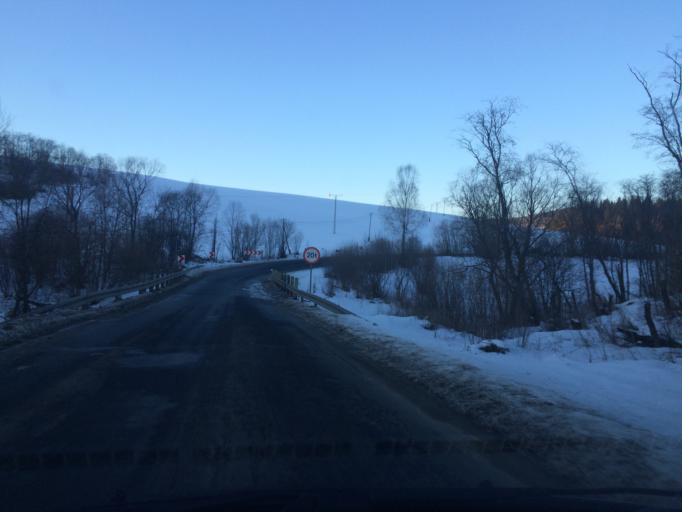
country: PL
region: Subcarpathian Voivodeship
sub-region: Powiat bieszczadzki
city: Lutowiska
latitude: 49.2377
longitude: 22.6986
